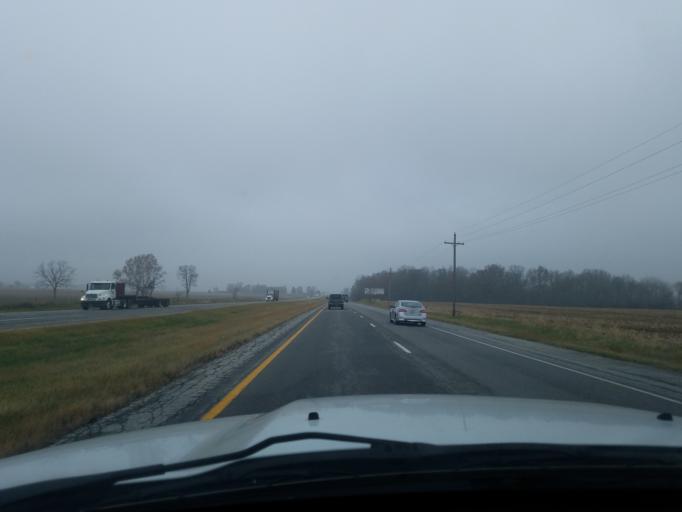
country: US
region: Indiana
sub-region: Howard County
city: Indian Heights
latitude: 40.3582
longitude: -86.1270
